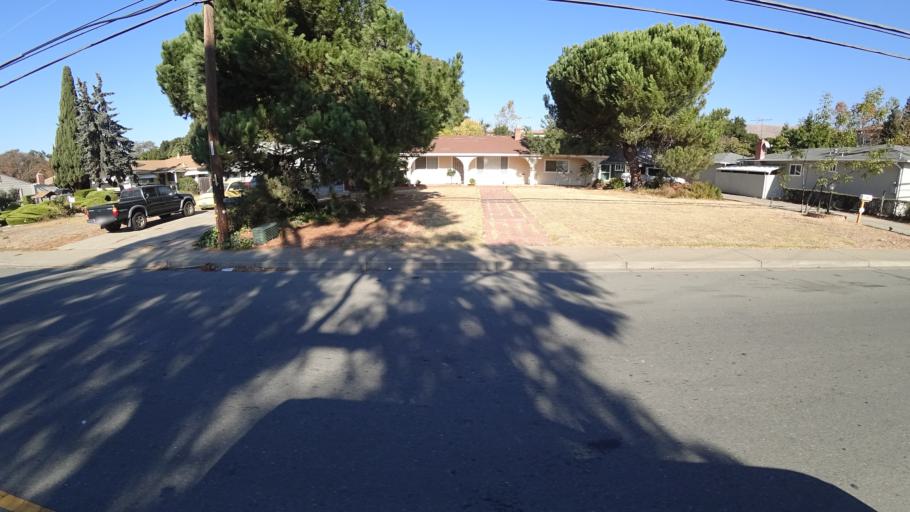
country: US
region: California
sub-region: Alameda County
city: Union City
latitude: 37.6059
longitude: -122.0220
